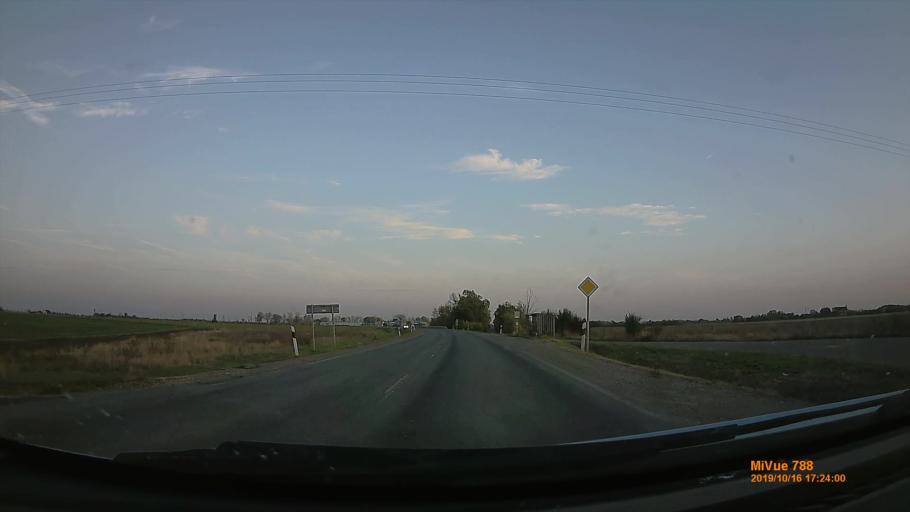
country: HU
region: Heves
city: Fuzesabony
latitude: 47.7684
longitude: 20.3845
